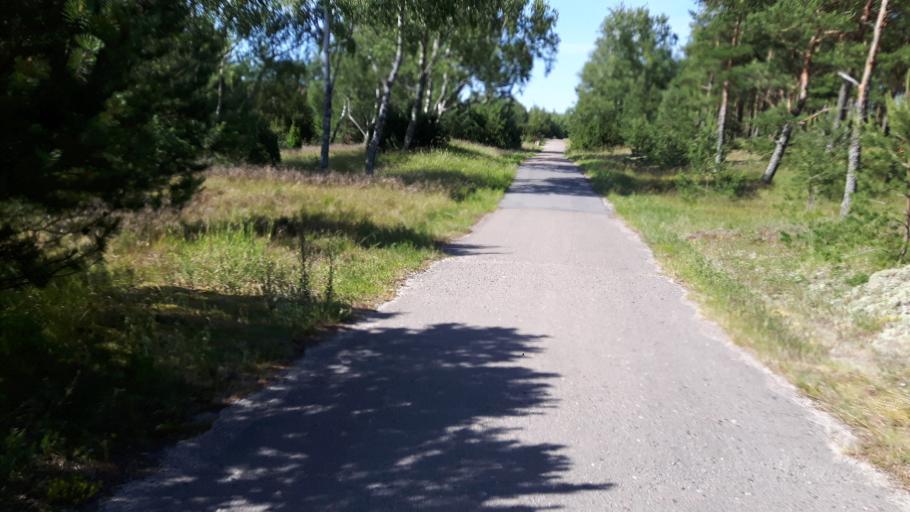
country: LT
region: Klaipedos apskritis
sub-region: Klaipeda
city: Klaipeda
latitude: 55.6899
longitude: 21.1032
